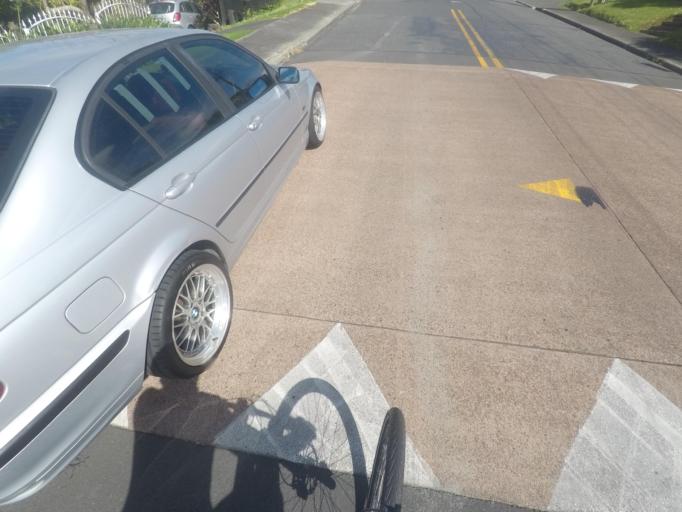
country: NZ
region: Auckland
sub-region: Auckland
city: Auckland
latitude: -36.9231
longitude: 174.7623
